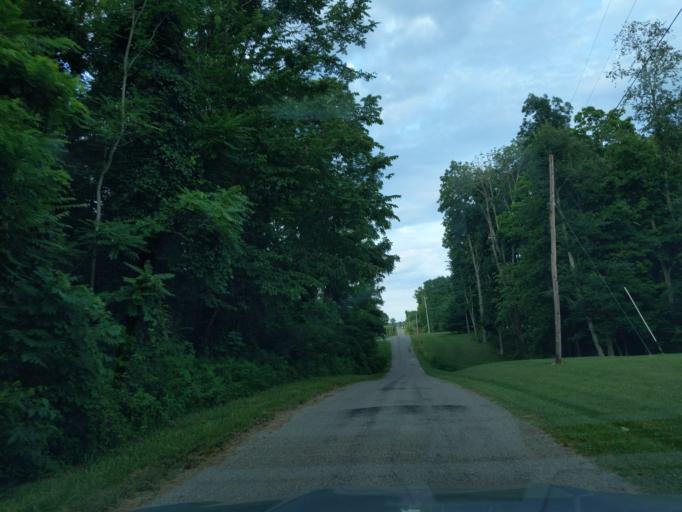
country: US
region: Indiana
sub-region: Ripley County
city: Sunman
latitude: 39.3100
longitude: -85.0831
